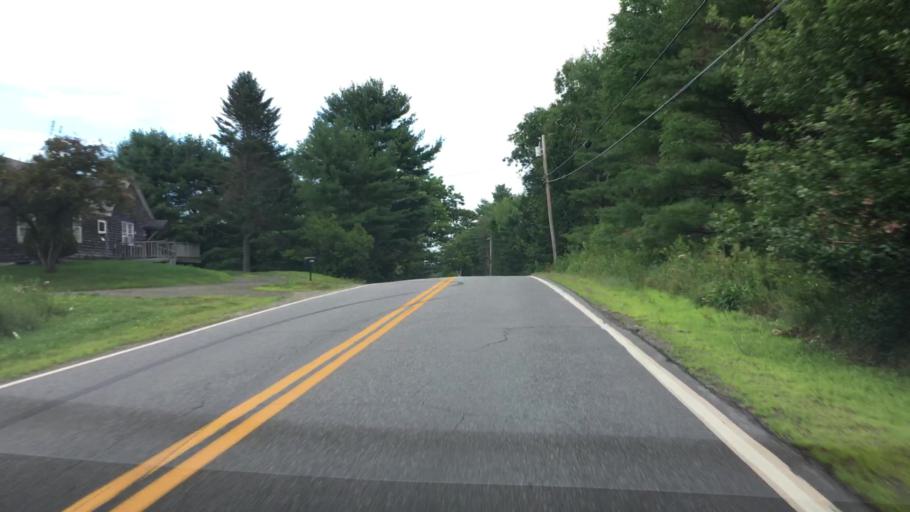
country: US
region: Maine
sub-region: Waldo County
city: Lincolnville
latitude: 44.3229
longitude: -69.0687
